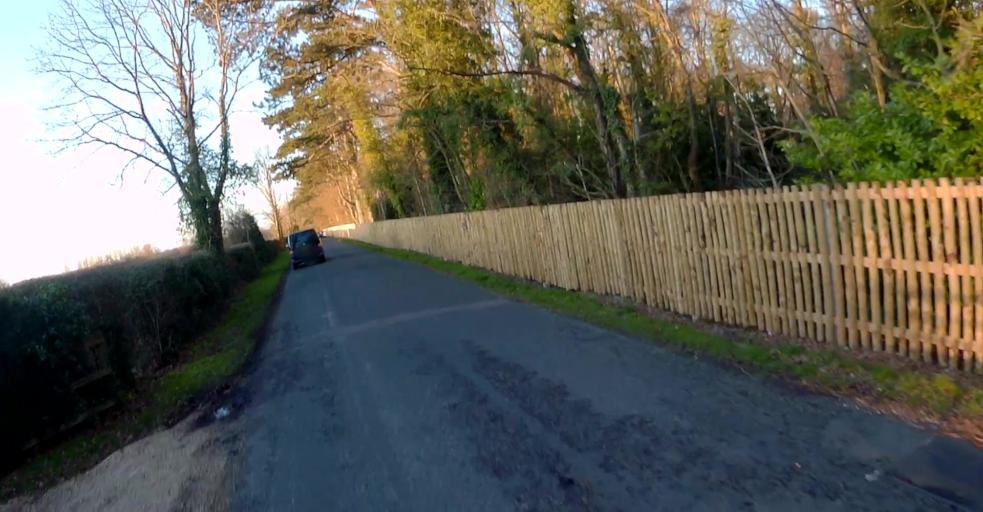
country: GB
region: England
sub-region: West Berkshire
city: Stratfield Mortimer
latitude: 51.3392
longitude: -1.0012
